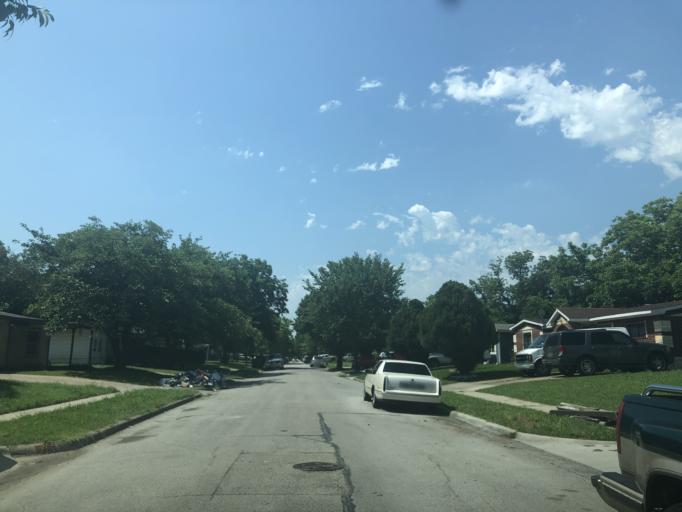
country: US
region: Texas
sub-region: Dallas County
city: Grand Prairie
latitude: 32.7316
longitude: -97.0121
